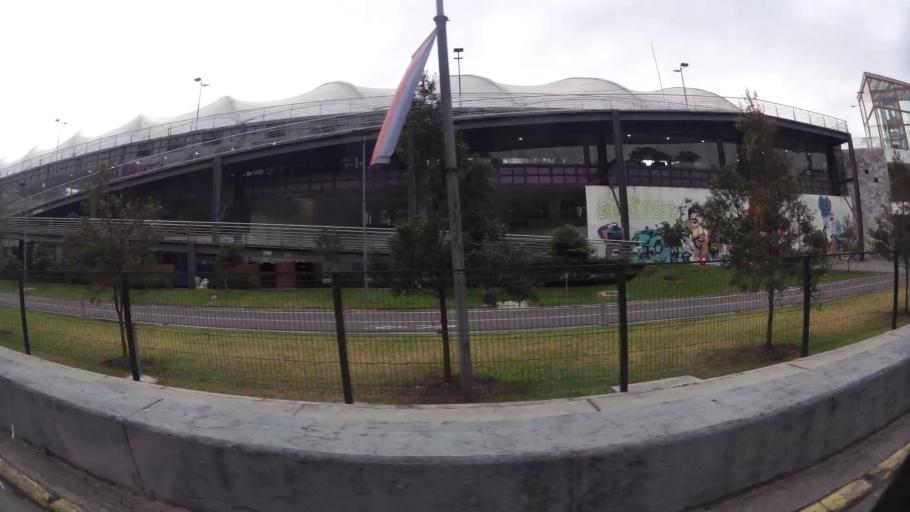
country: EC
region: Pichincha
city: Quito
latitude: -0.2289
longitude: -78.5117
